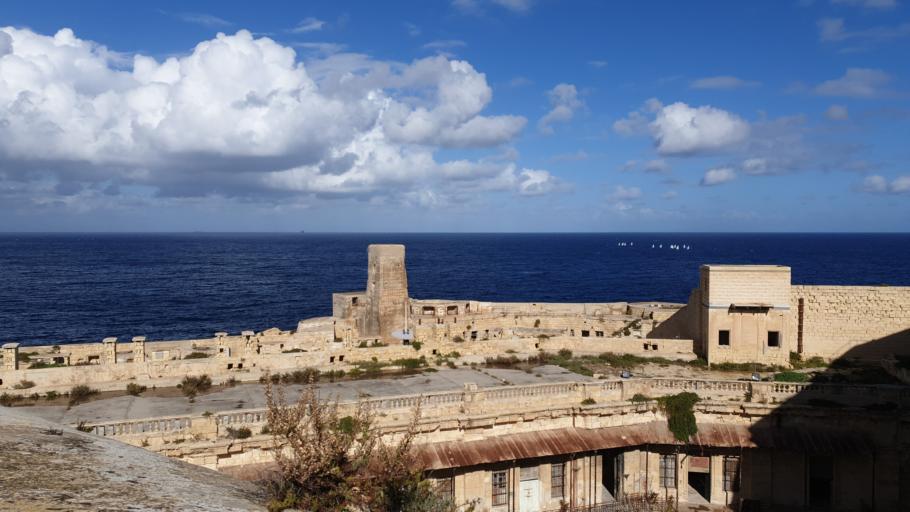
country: MT
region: Il-Belt Valletta
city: Valletta
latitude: 35.9024
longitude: 14.5184
